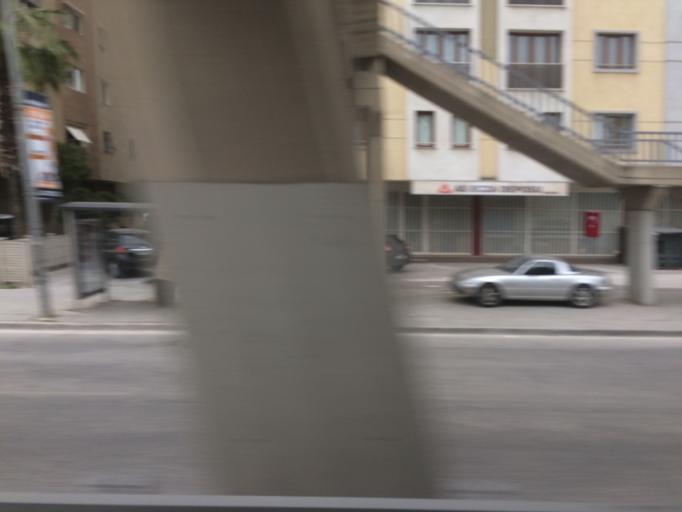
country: TR
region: Izmir
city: Bornova
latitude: 38.4543
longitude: 27.1968
